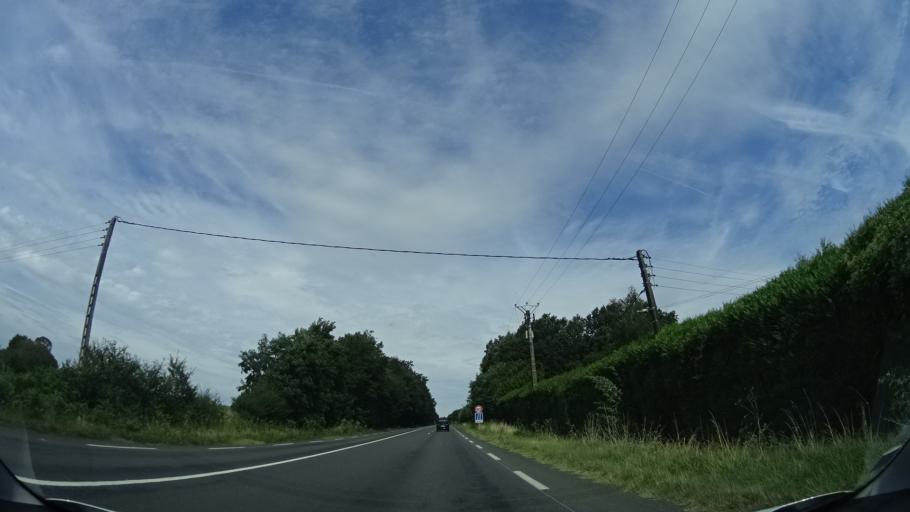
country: FR
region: Pays de la Loire
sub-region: Departement de la Sarthe
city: La Fleche
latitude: 47.7261
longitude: -0.1121
